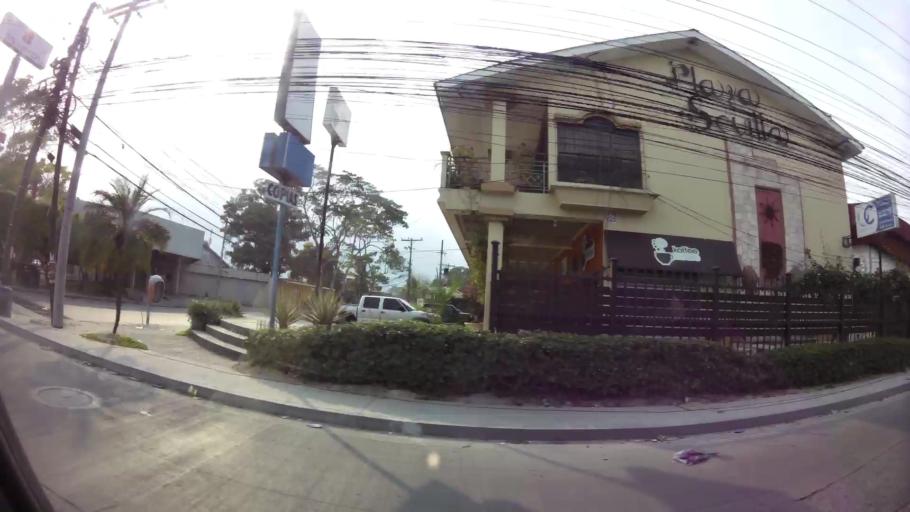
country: HN
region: Cortes
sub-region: San Pedro Sula
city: Pena Blanca
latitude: 15.5457
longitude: -88.0129
